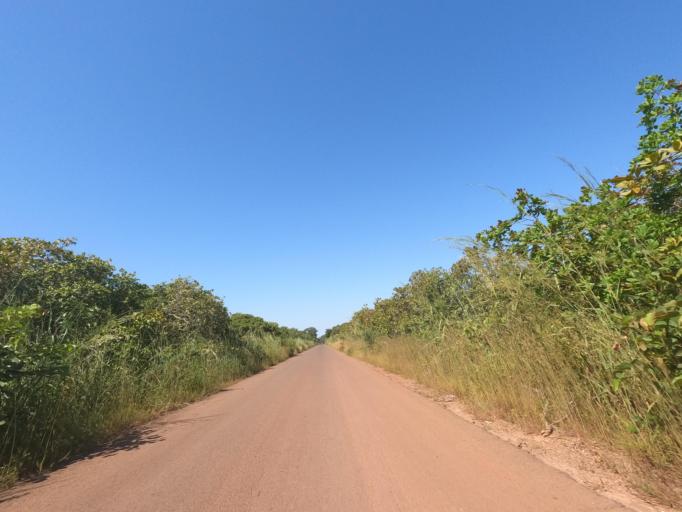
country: GW
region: Cacheu
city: Cacheu
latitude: 12.4092
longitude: -16.0258
